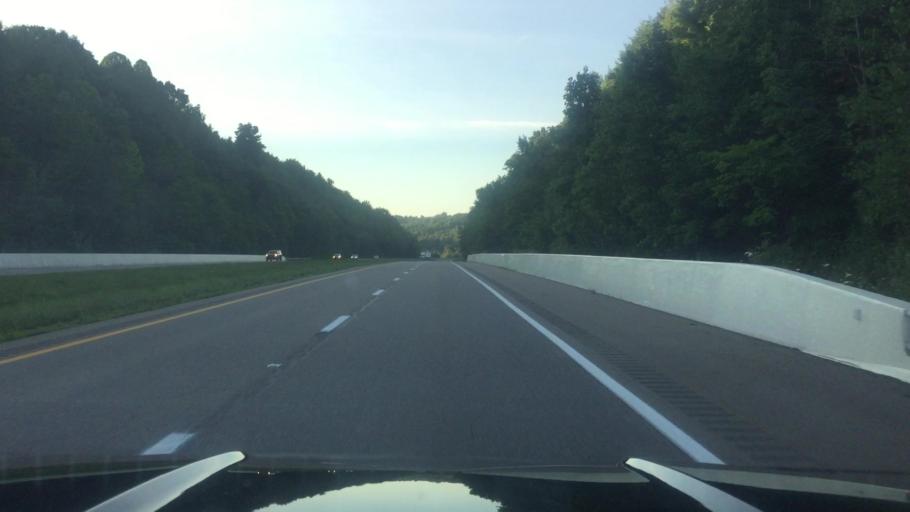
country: US
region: Ohio
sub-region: Tuscarawas County
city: Newcomerstown
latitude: 40.2264
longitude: -81.5535
